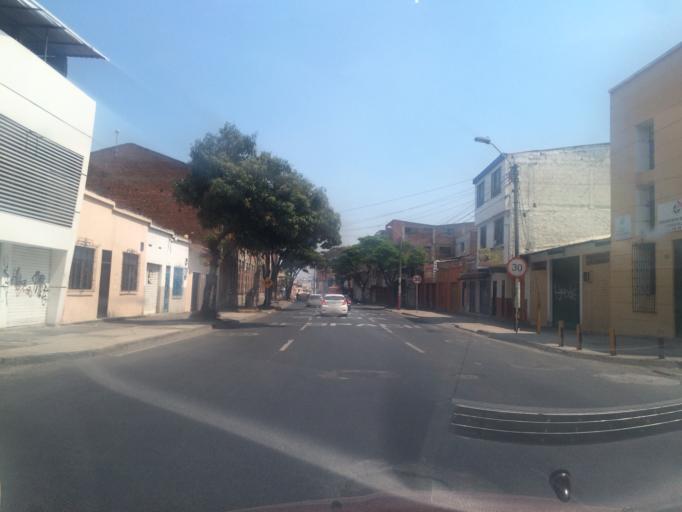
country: CO
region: Valle del Cauca
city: Cali
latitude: 3.4437
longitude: -76.5342
